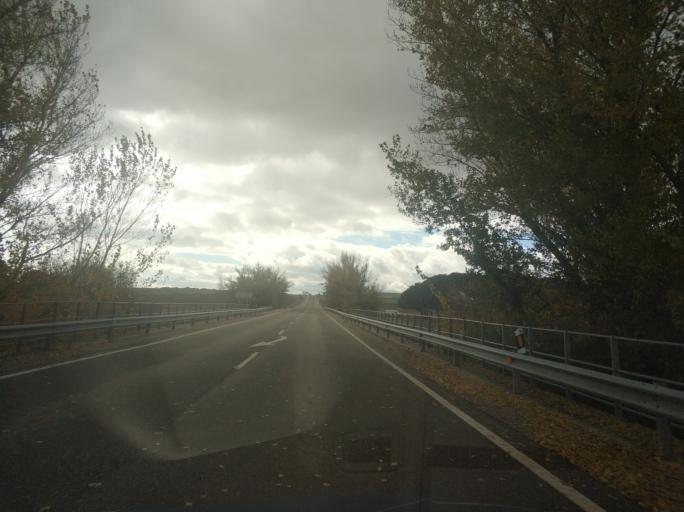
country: ES
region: Castille and Leon
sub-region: Provincia de Zamora
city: Castrillo de la Guarena
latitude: 41.2293
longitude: -5.3115
